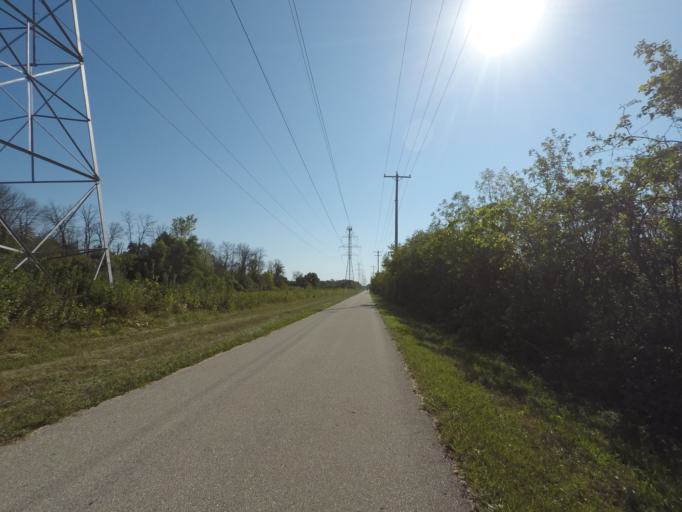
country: US
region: Wisconsin
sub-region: Waukesha County
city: New Berlin
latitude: 43.0101
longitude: -88.1486
